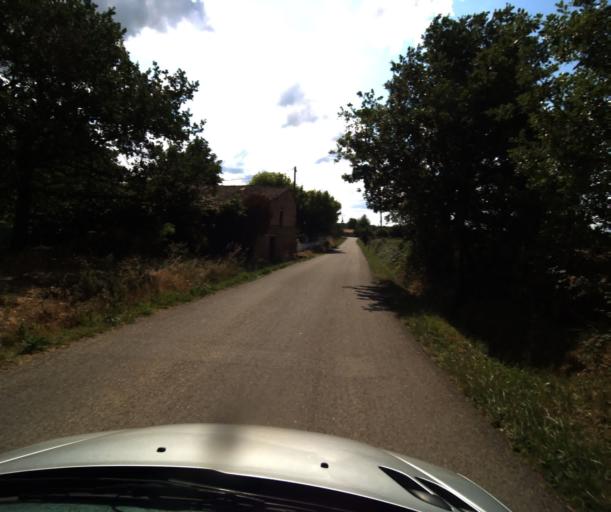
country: FR
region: Midi-Pyrenees
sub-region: Departement du Tarn-et-Garonne
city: Campsas
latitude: 43.8963
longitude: 1.3038
